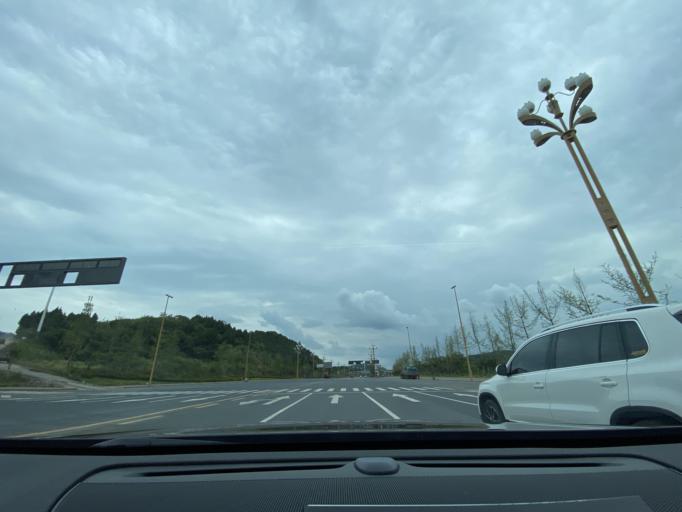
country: CN
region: Sichuan
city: Jiancheng
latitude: 30.4660
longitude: 104.4950
